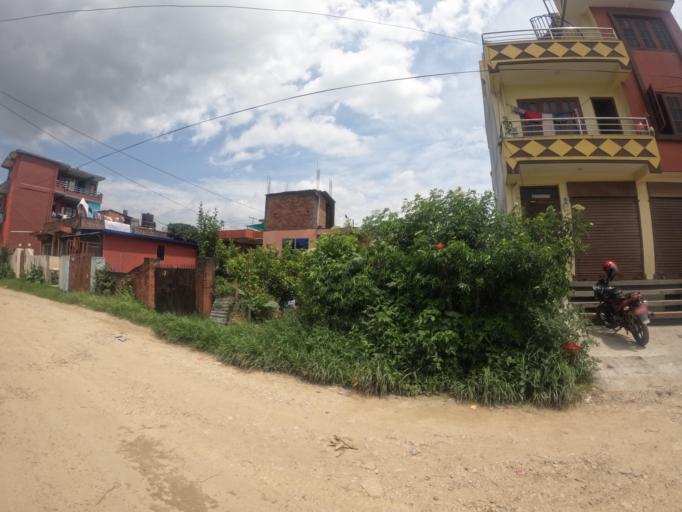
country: NP
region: Central Region
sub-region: Bagmati Zone
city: Bhaktapur
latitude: 27.6854
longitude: 85.3780
